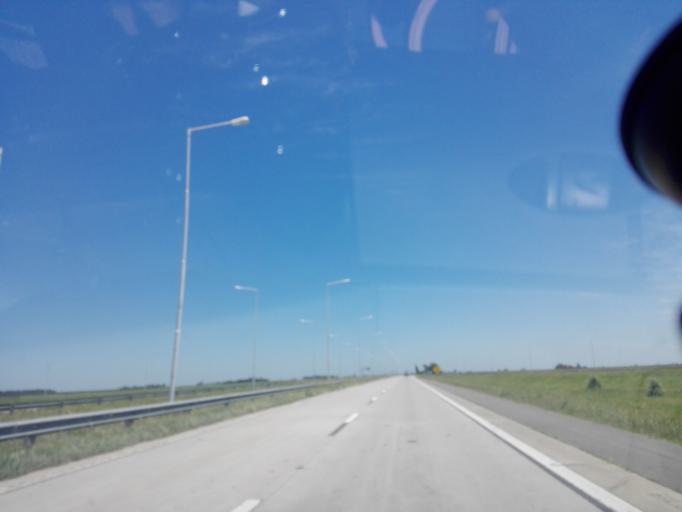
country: AR
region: Cordoba
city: Leones
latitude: -32.6302
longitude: -62.2892
